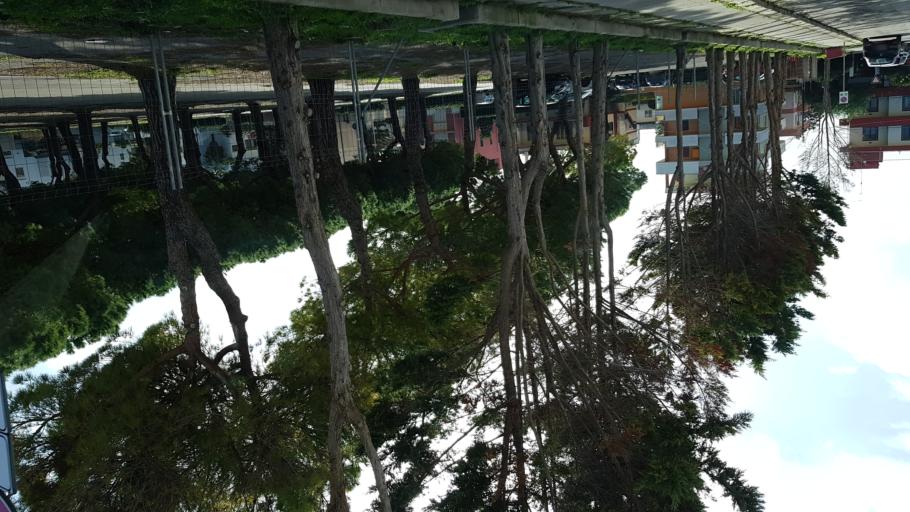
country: IT
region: Apulia
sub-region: Provincia di Brindisi
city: Brindisi
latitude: 40.6485
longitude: 17.9376
